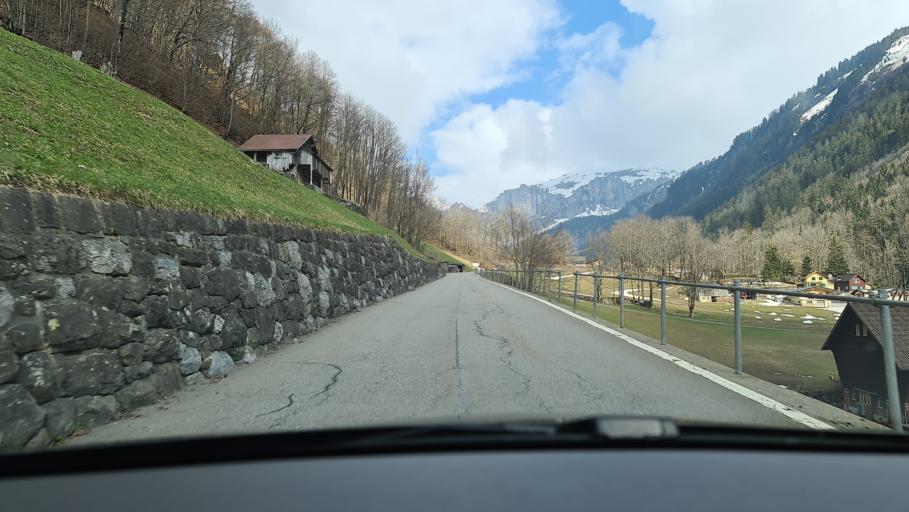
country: CH
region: Uri
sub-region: Uri
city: Burglen
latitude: 46.8648
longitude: 8.7756
